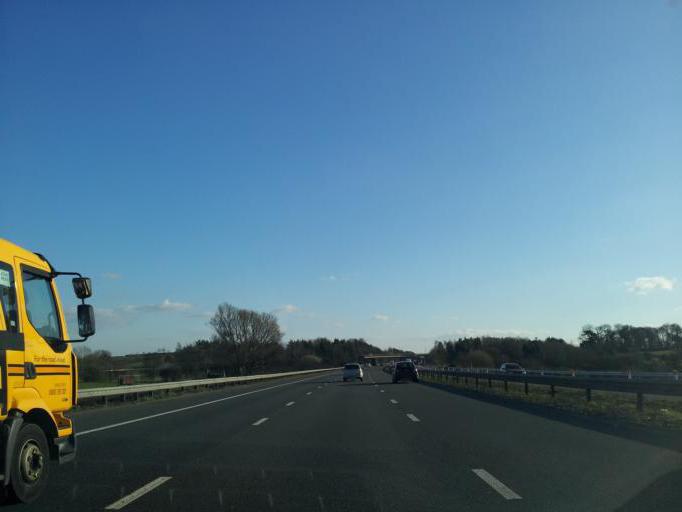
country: GB
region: England
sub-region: Devon
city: Heavitree
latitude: 50.7547
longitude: -3.4561
